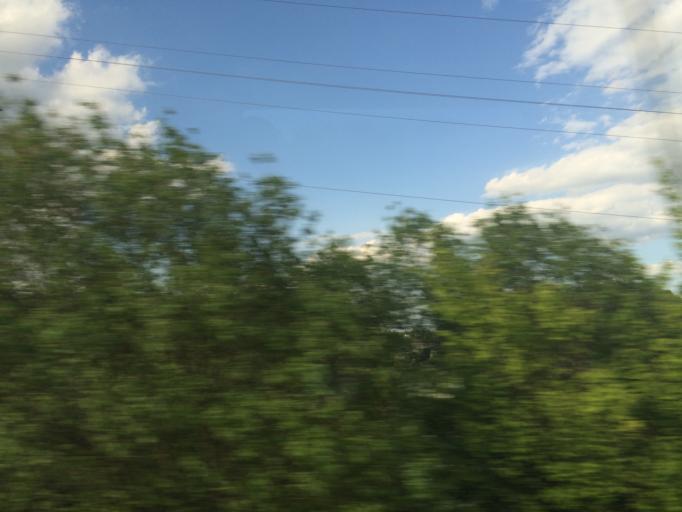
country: DE
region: Rheinland-Pfalz
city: Urbach-Uberdorf
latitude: 50.5549
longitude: 7.5690
